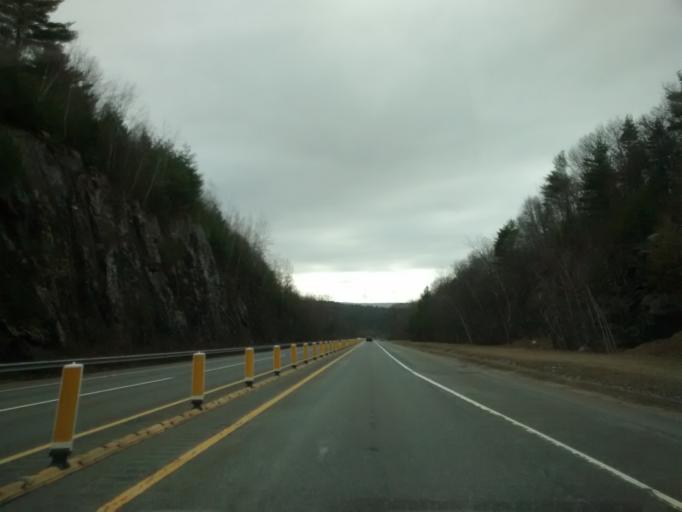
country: US
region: Massachusetts
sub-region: Worcester County
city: Athol
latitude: 42.5637
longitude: -72.2348
